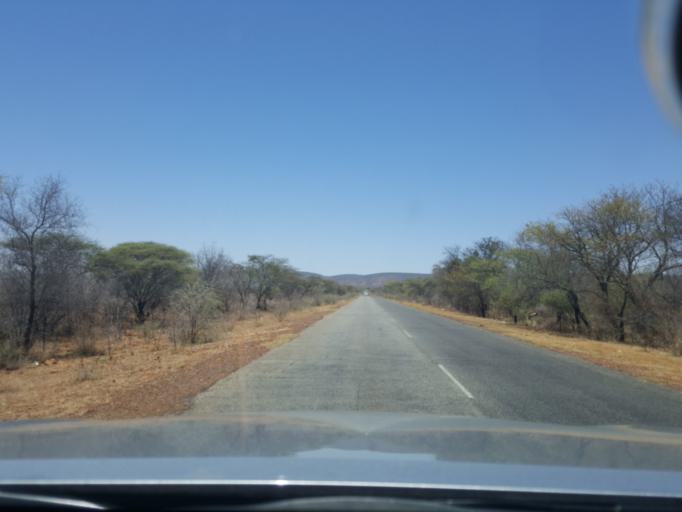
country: BW
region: South East
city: Lobatse
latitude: -25.2382
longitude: 25.9351
